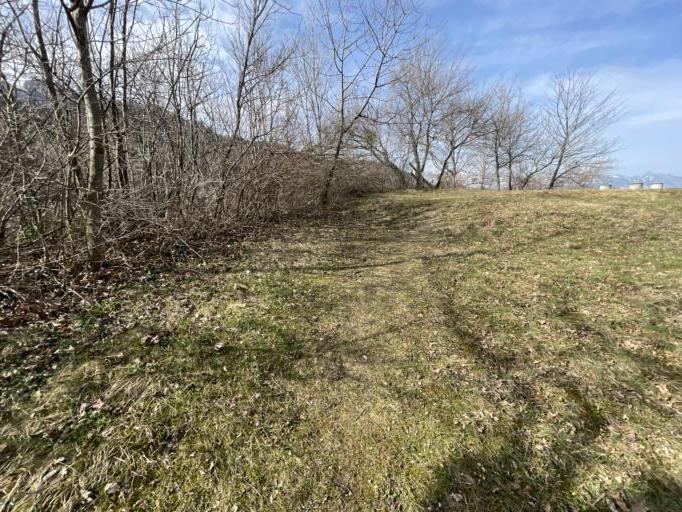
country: CH
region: Saint Gallen
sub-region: Wahlkreis Werdenberg
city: Sevelen
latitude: 47.1203
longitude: 9.4869
